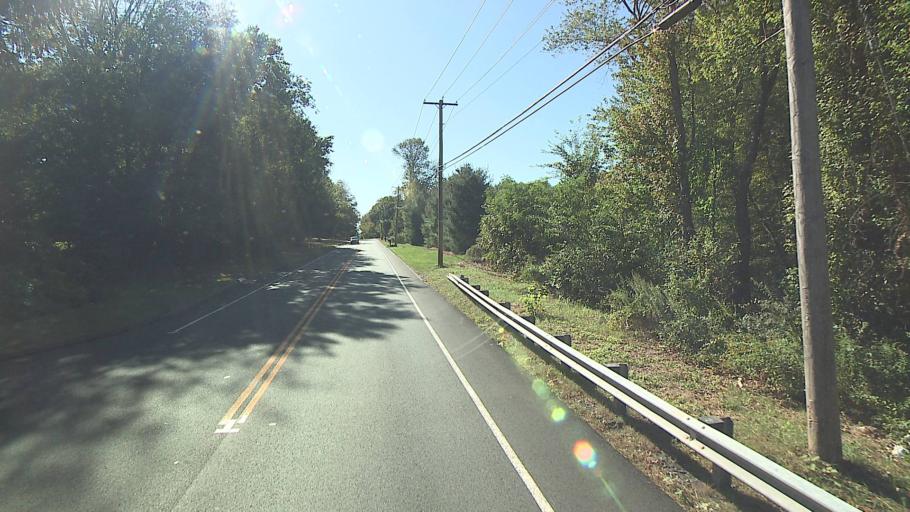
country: US
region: Connecticut
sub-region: New Haven County
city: Orange
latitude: 41.2887
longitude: -73.0131
